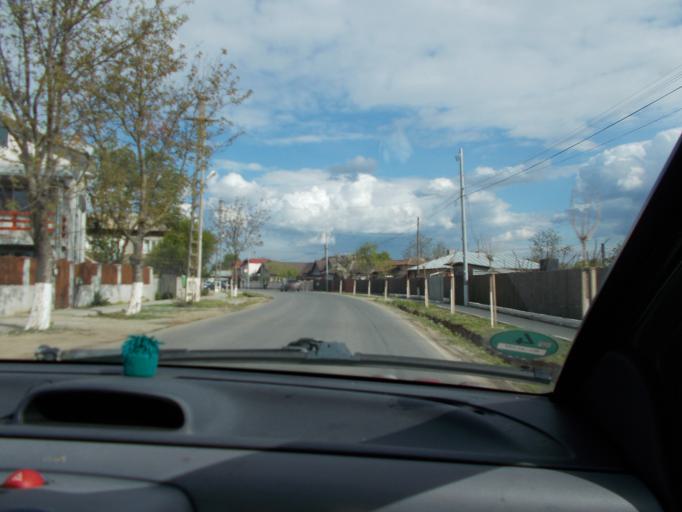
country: RO
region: Ilfov
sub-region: Comuna Branesti
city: Branesti
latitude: 44.4604
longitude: 26.3311
